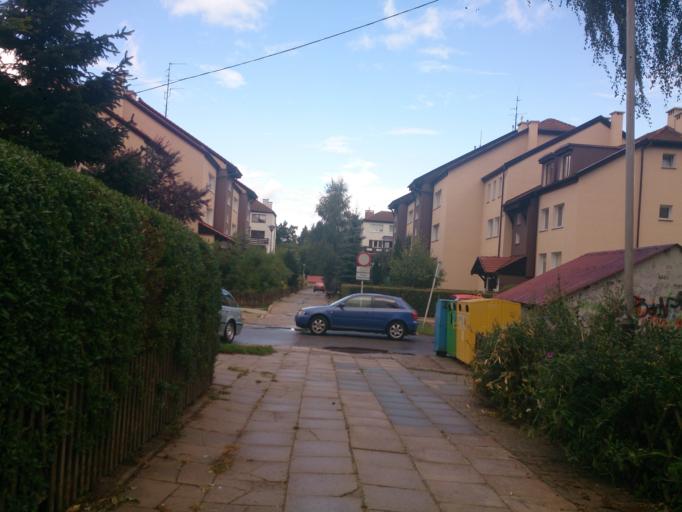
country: PL
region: Pomeranian Voivodeship
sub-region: Sopot
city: Sopot
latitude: 54.3785
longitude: 18.5054
